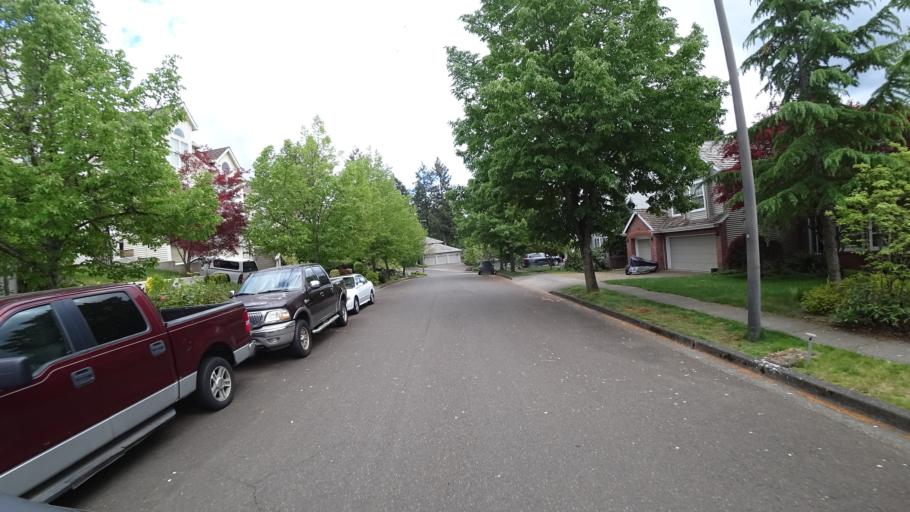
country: US
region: Oregon
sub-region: Washington County
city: Aloha
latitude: 45.4710
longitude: -122.8457
